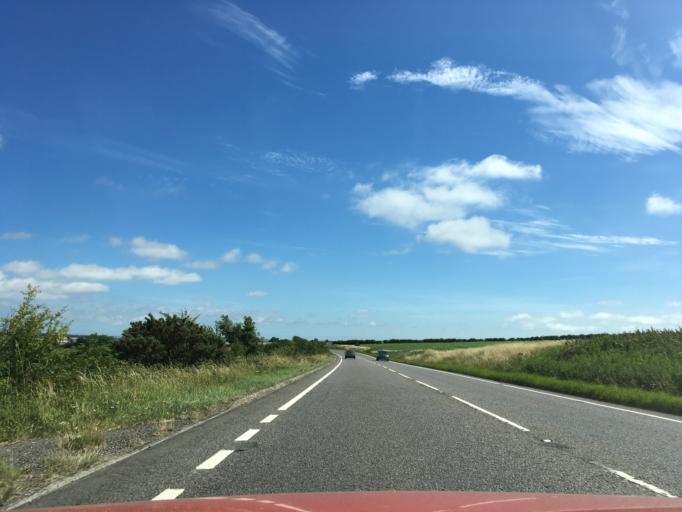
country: GB
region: England
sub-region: Dorset
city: Dorchester
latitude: 50.7936
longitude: -2.5478
